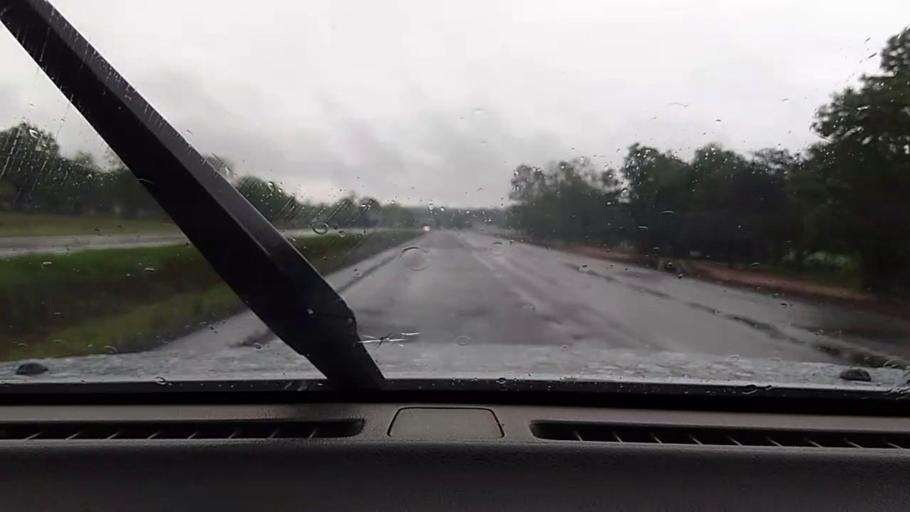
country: PY
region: Caaguazu
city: Repatriacion
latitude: -25.4644
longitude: -55.9308
